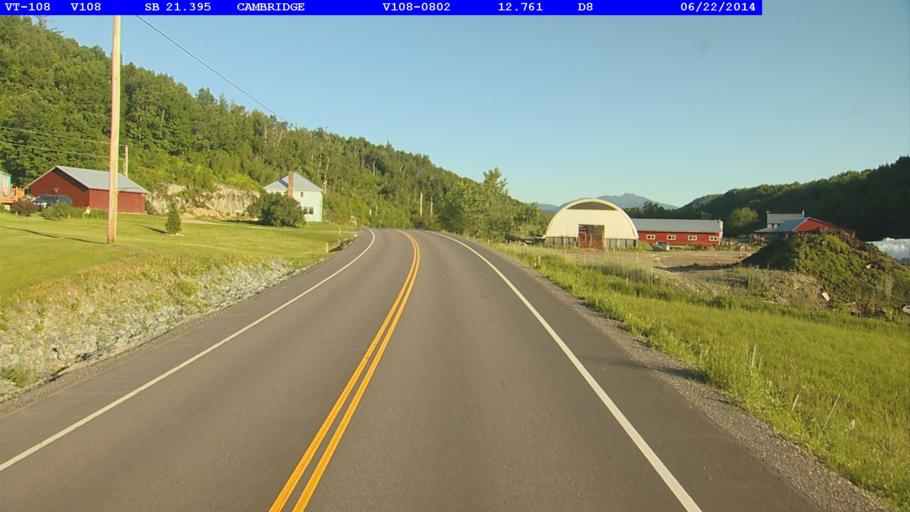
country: US
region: Vermont
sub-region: Lamoille County
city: Johnson
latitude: 44.6988
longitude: -72.8292
